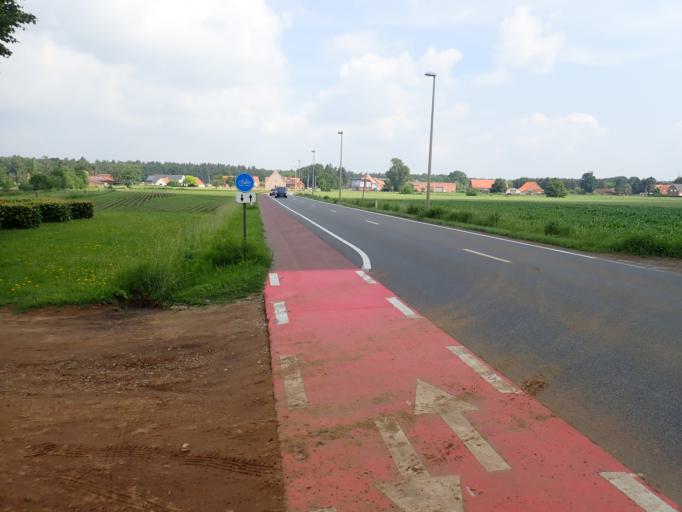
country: BE
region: Flanders
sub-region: Provincie Antwerpen
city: Herentals
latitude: 51.2073
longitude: 4.8182
